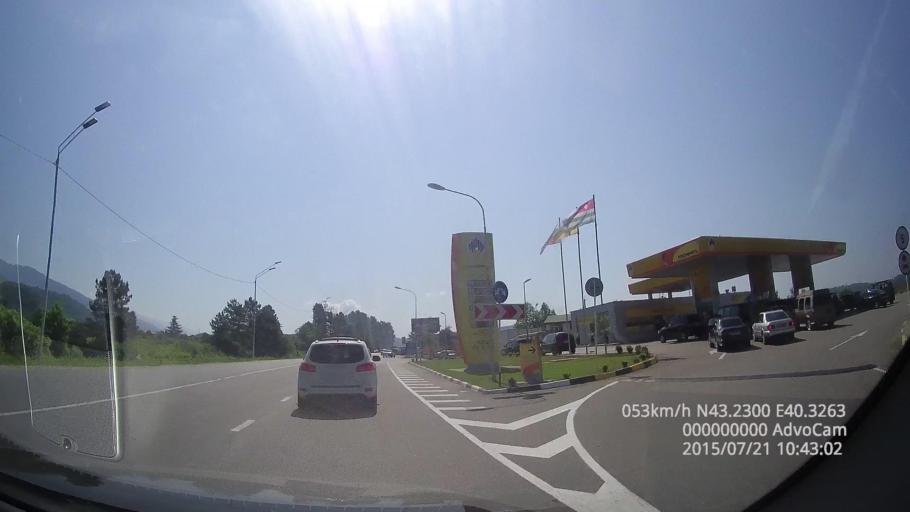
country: GE
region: Abkhazia
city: Bich'vinta
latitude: 43.2299
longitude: 40.3267
